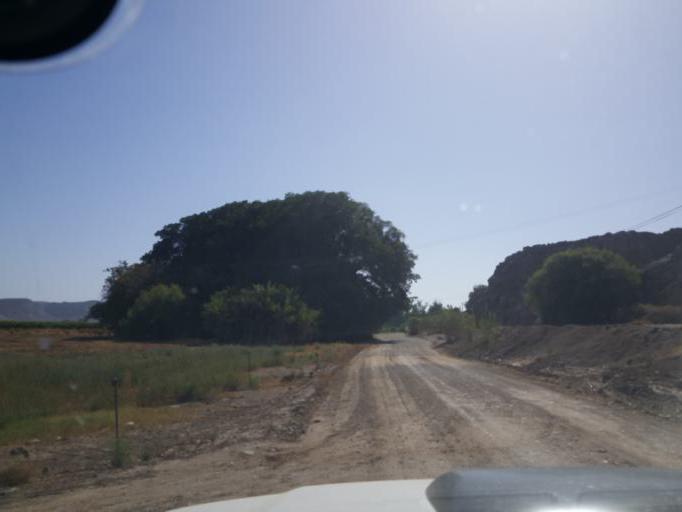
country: ZA
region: Northern Cape
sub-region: Namakwa District Municipality
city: Port Nolloth
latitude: -28.6991
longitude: 17.5618
